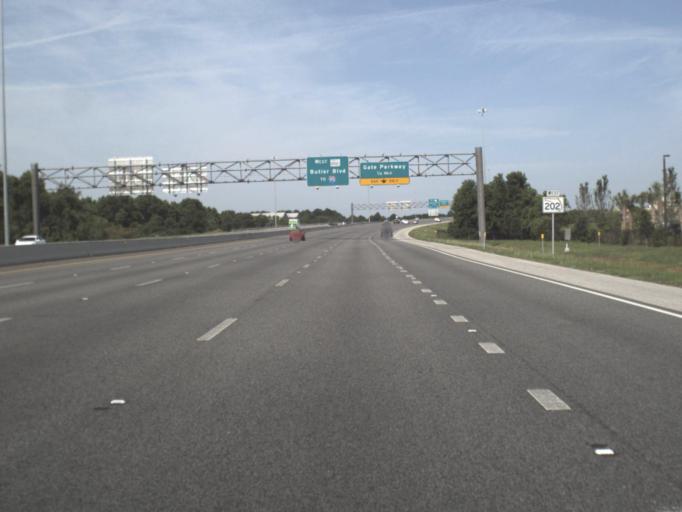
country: US
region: Florida
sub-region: Duval County
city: Jacksonville Beach
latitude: 30.2511
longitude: -81.5258
